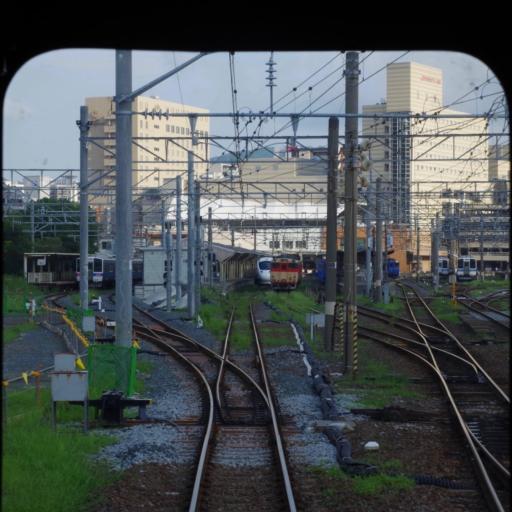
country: JP
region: Nagasaki
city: Nagasaki-shi
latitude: 32.7556
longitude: 129.8688
